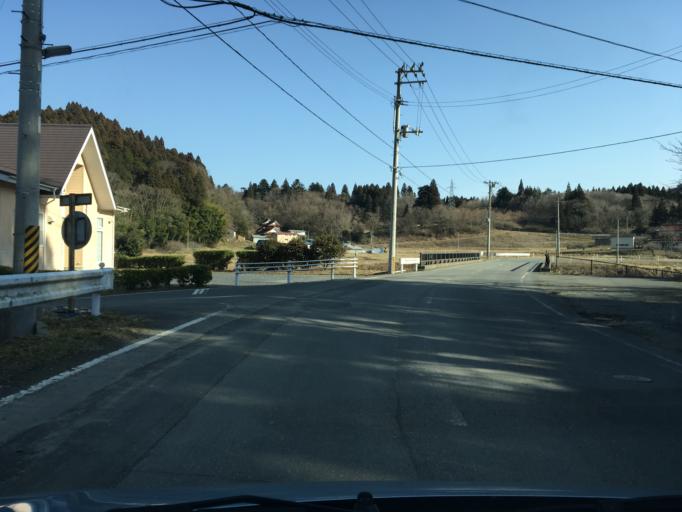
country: JP
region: Miyagi
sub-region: Oshika Gun
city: Onagawa Cho
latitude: 38.7868
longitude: 141.4584
